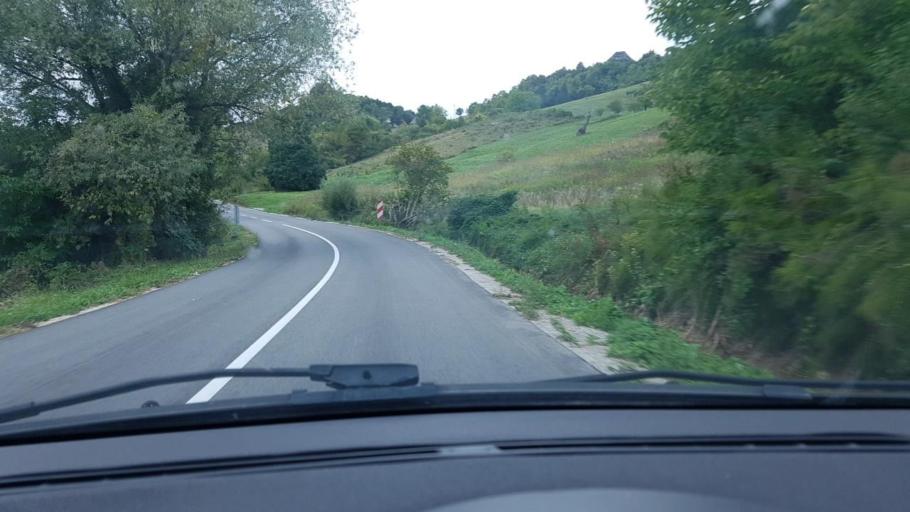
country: SI
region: Podcetrtek
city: Podcetrtek
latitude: 46.1513
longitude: 15.6537
